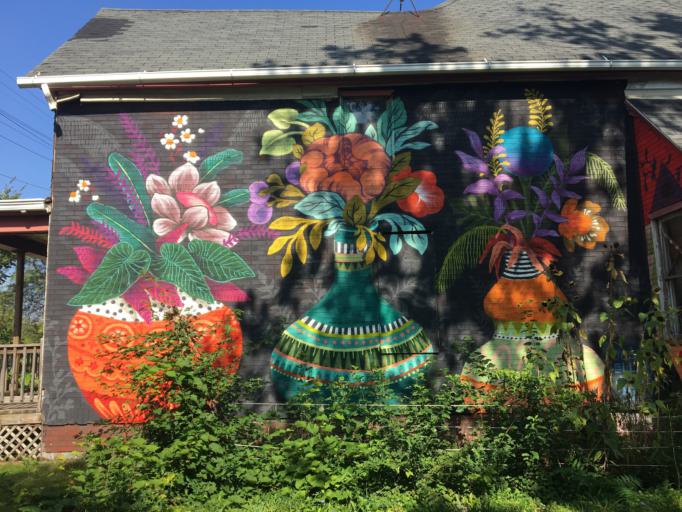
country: US
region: Michigan
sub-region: Wayne County
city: Hamtramck
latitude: 42.3727
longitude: -83.0100
